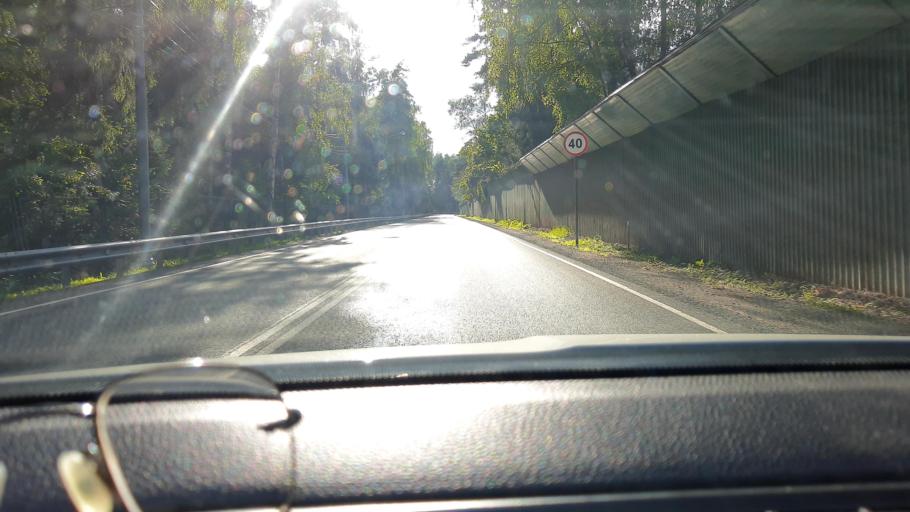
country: RU
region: Moskovskaya
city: Nikolina Gora
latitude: 55.7165
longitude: 36.9670
